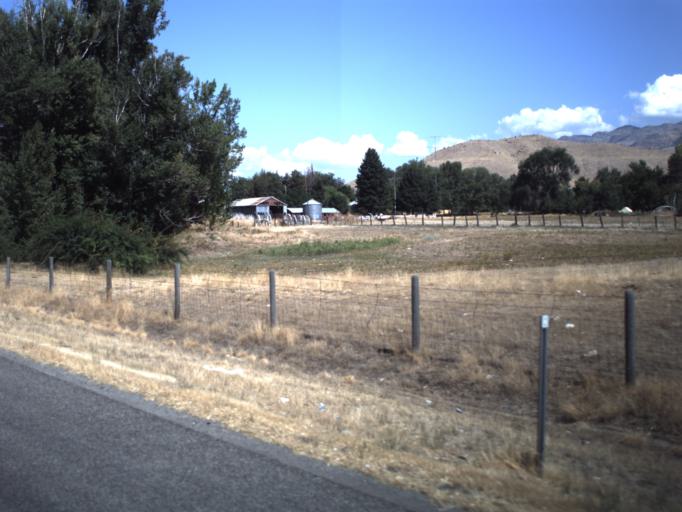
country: US
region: Utah
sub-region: Cache County
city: Richmond
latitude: 41.9500
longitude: -111.8133
